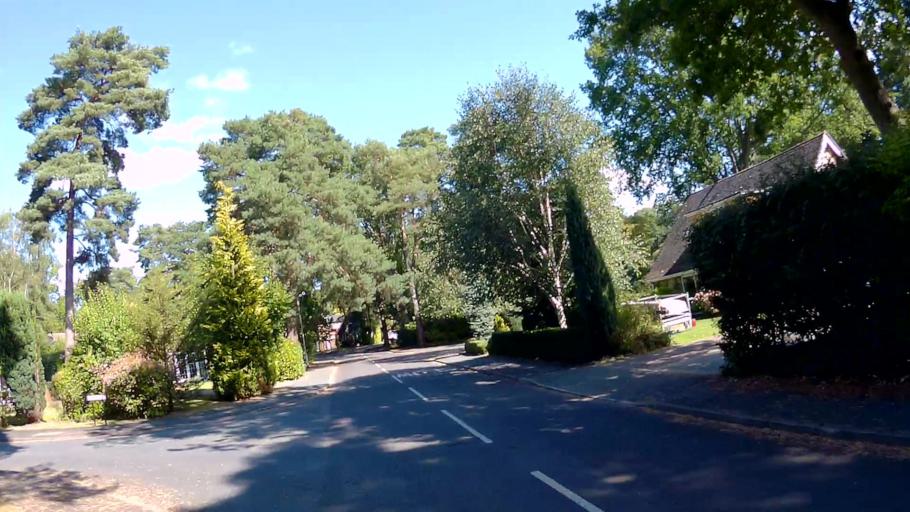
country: GB
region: England
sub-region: Bracknell Forest
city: Crowthorne
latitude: 51.3705
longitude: -0.8086
